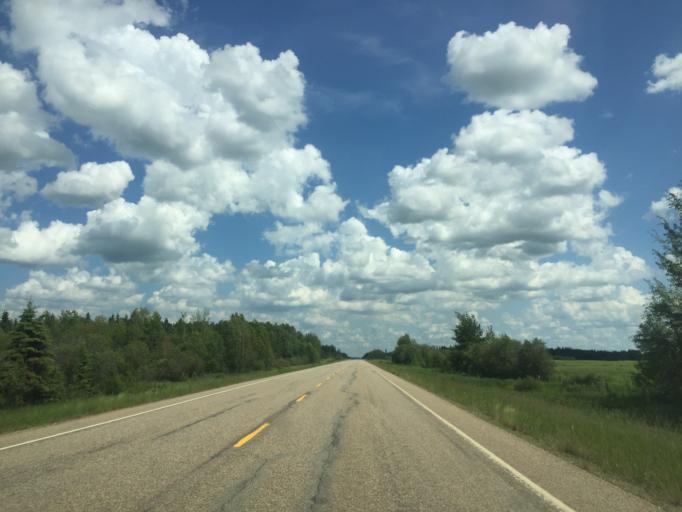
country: CA
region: Alberta
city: Athabasca
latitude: 54.3267
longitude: -113.2385
